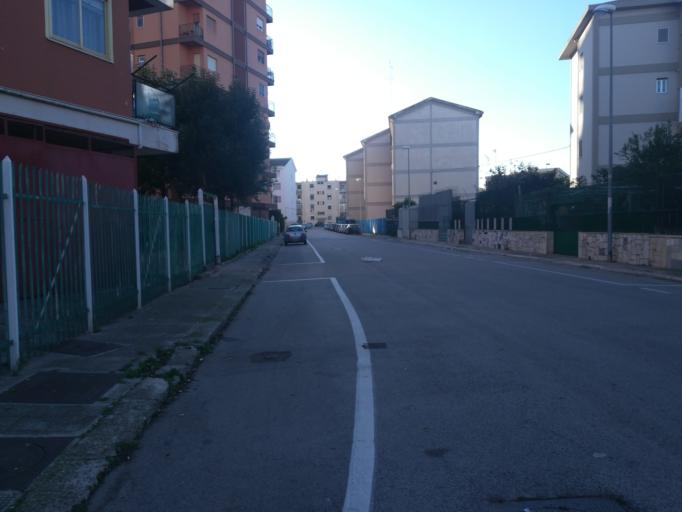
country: IT
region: Apulia
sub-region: Provincia di Bari
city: San Paolo
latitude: 41.1220
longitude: 16.7916
